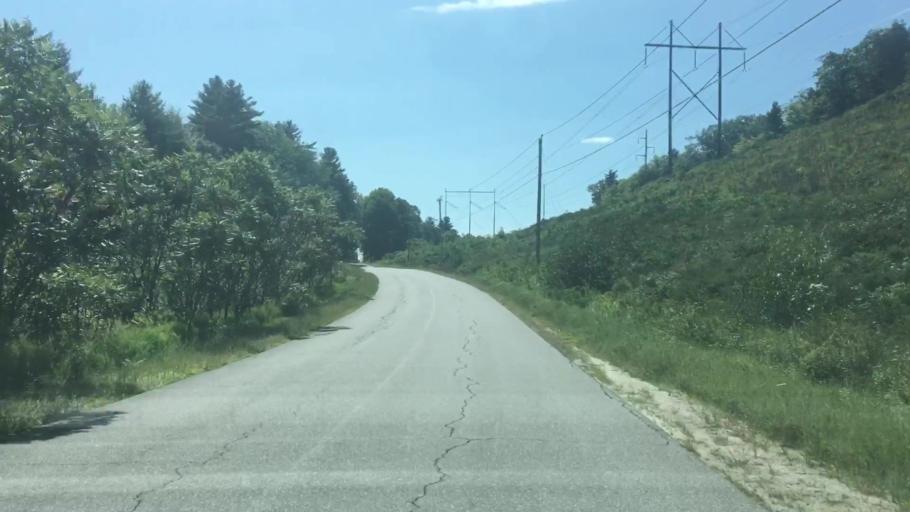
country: US
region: Maine
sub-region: Kennebec County
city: Monmouth
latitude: 44.1994
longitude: -69.9621
